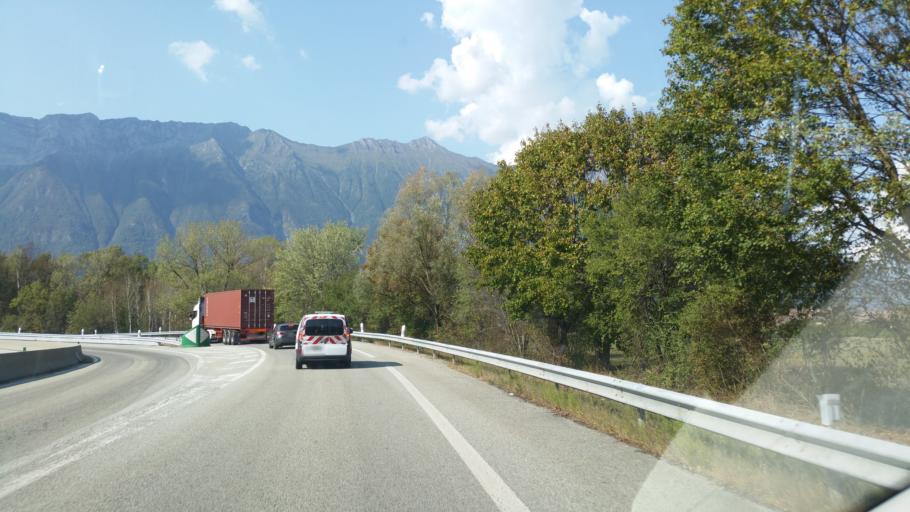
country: FR
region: Rhone-Alpes
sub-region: Departement de la Savoie
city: Aiton
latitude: 45.5572
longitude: 6.2451
